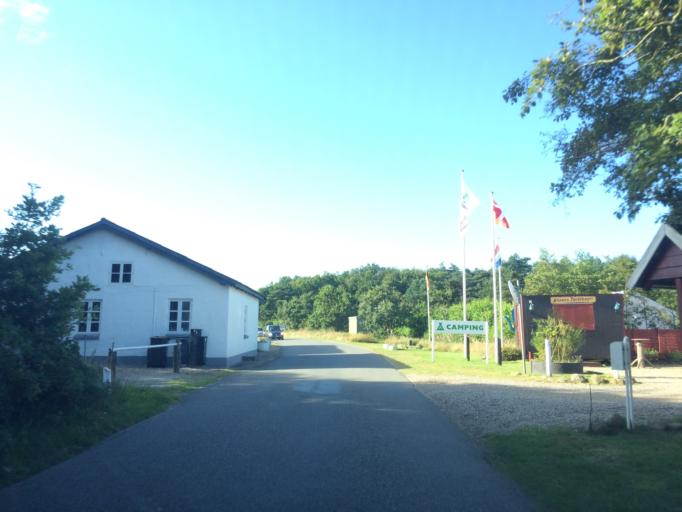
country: DK
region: Central Jutland
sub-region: Ringkobing-Skjern Kommune
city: Hvide Sande
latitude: 55.8270
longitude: 8.2156
